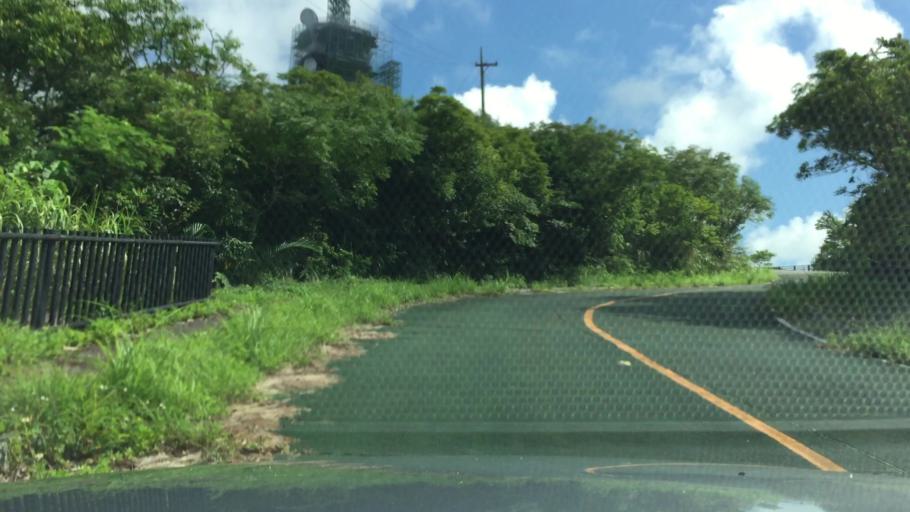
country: JP
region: Okinawa
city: Ishigaki
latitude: 24.3778
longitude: 124.1644
